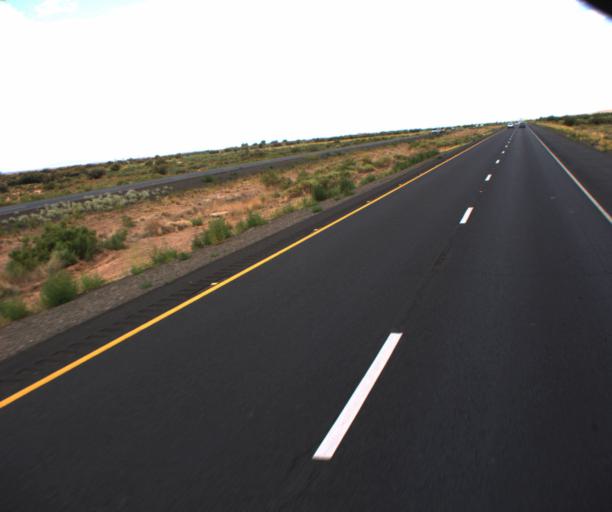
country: US
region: Arizona
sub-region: Navajo County
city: Winslow
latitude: 34.9842
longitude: -110.5515
